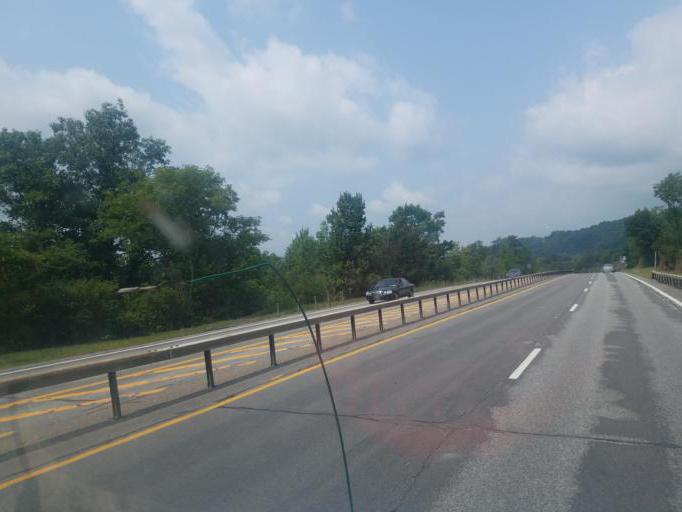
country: US
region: New York
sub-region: Herkimer County
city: Little Falls
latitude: 43.0404
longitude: -74.8419
